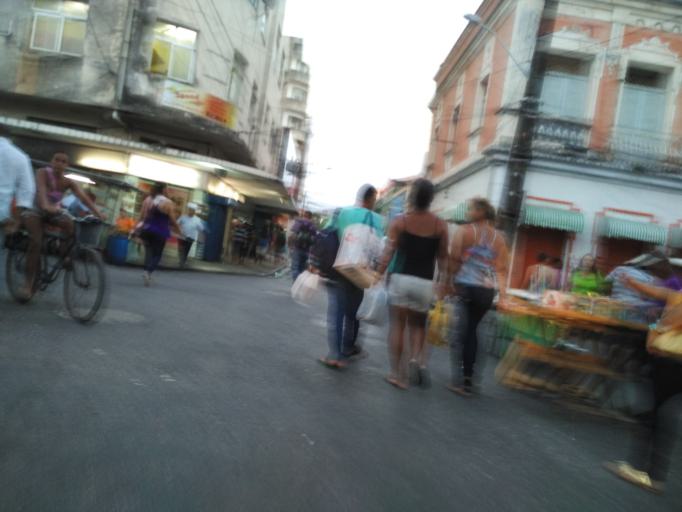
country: BR
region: Pernambuco
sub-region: Recife
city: Recife
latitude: -8.0672
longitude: -34.8812
